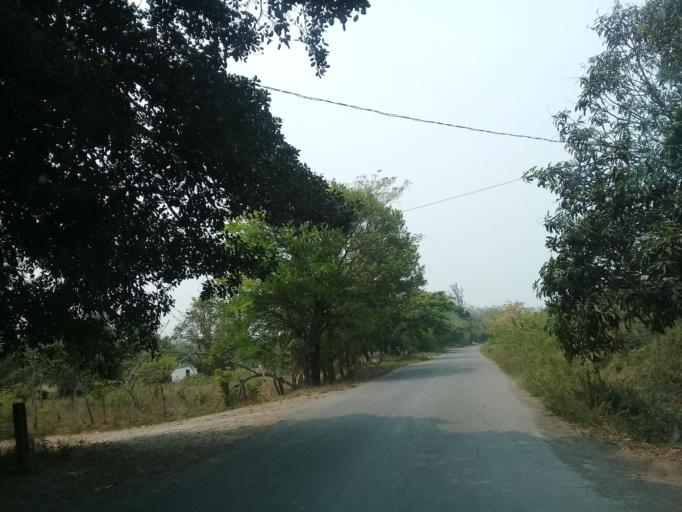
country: MX
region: Veracruz
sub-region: Medellin
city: La Laguna y Monte del Castillo
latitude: 18.9471
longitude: -96.1264
